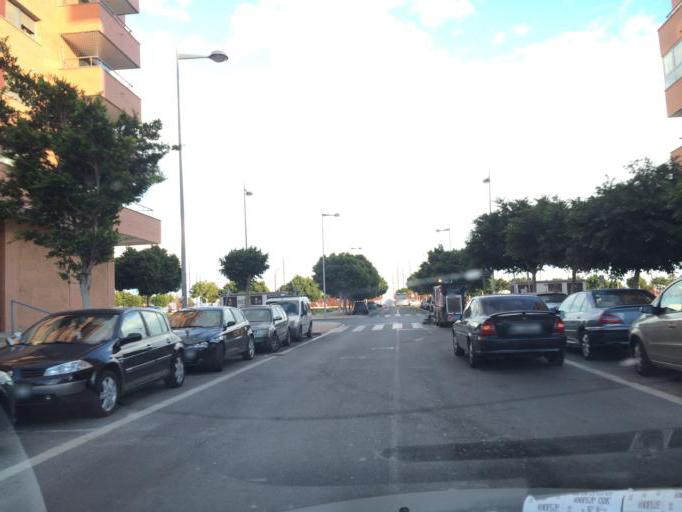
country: ES
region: Andalusia
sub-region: Provincia de Almeria
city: Almeria
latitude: 36.8367
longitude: -2.4336
